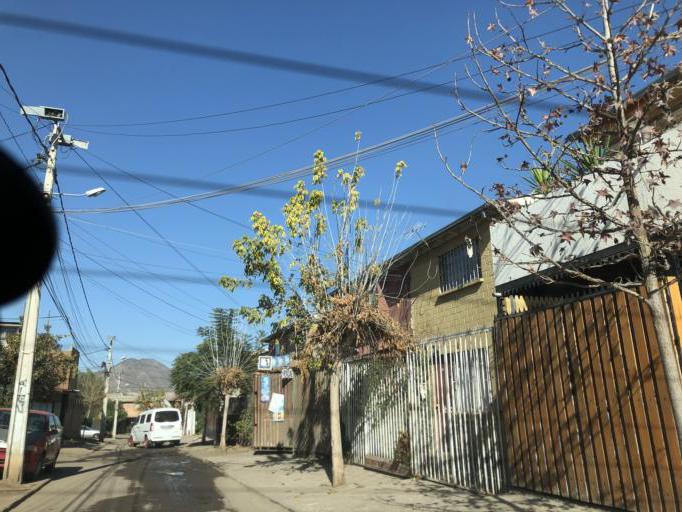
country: CL
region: Santiago Metropolitan
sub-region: Provincia de Santiago
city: La Pintana
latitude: -33.6225
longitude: -70.6267
